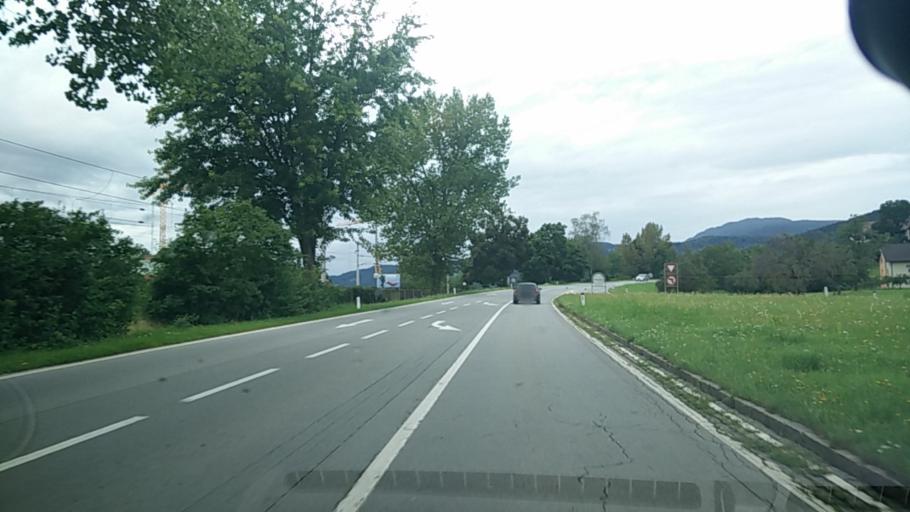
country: AT
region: Carinthia
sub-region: Politischer Bezirk Klagenfurt Land
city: Maria Worth
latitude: 46.6292
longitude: 14.1678
